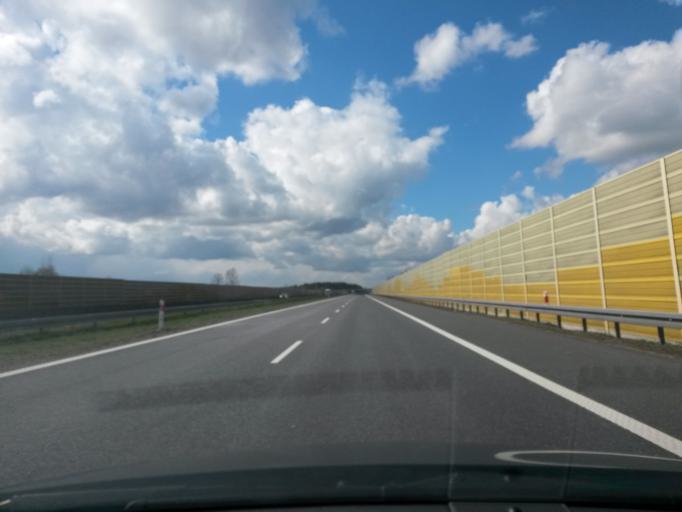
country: PL
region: Lodz Voivodeship
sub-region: Powiat leczycki
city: Swinice Warckie
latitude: 52.0296
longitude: 18.8999
